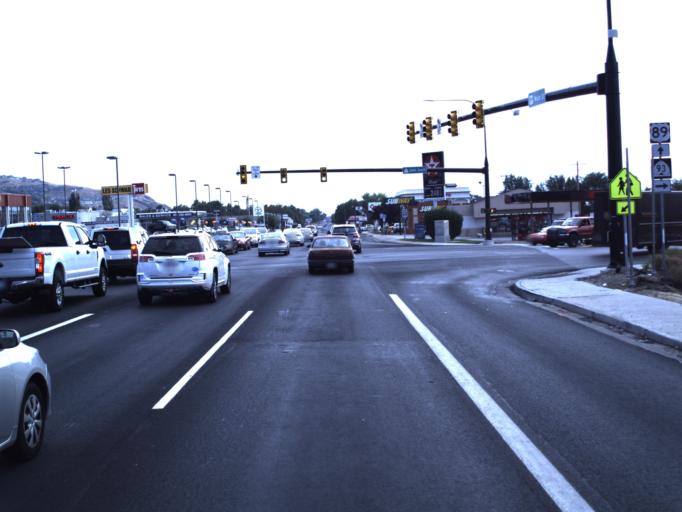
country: US
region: Utah
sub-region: Davis County
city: Woods Cross
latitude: 40.8620
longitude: -111.8961
